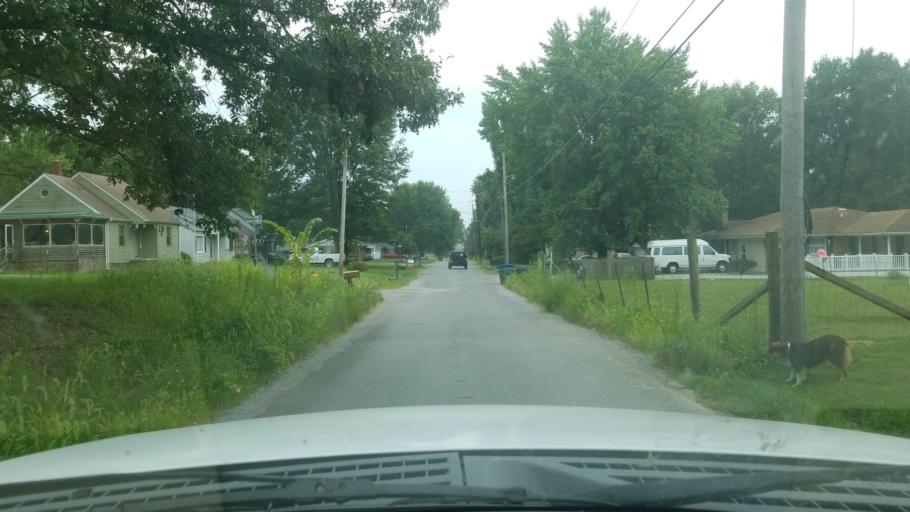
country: US
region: Illinois
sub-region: Saline County
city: Eldorado
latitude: 37.8206
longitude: -88.4476
